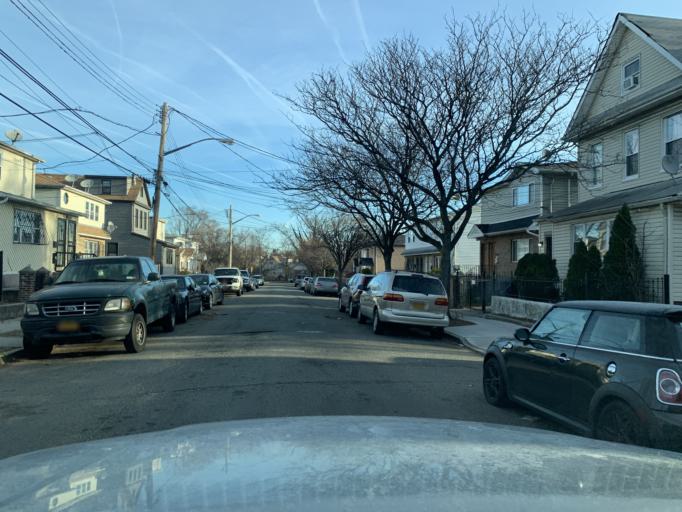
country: US
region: New York
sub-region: Queens County
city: Jamaica
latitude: 40.6907
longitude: -73.7859
